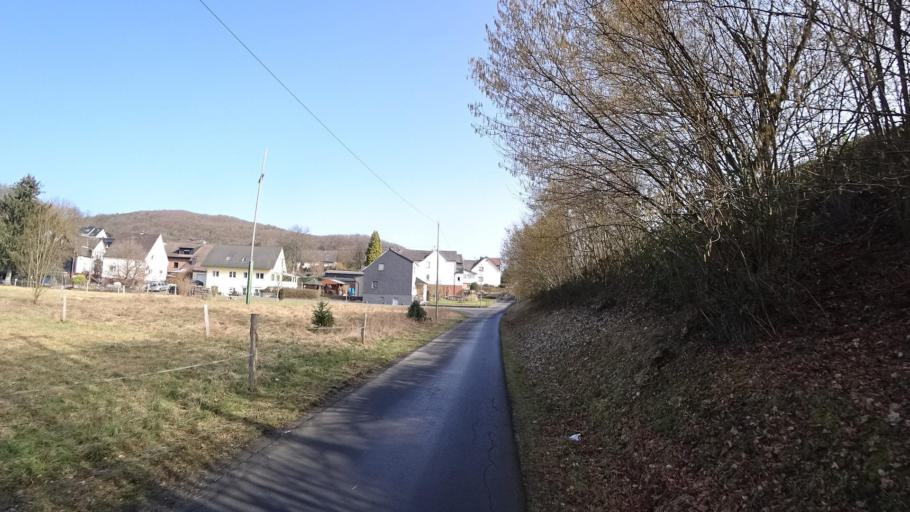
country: DE
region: Rheinland-Pfalz
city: Furthen
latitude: 50.7820
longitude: 7.6742
